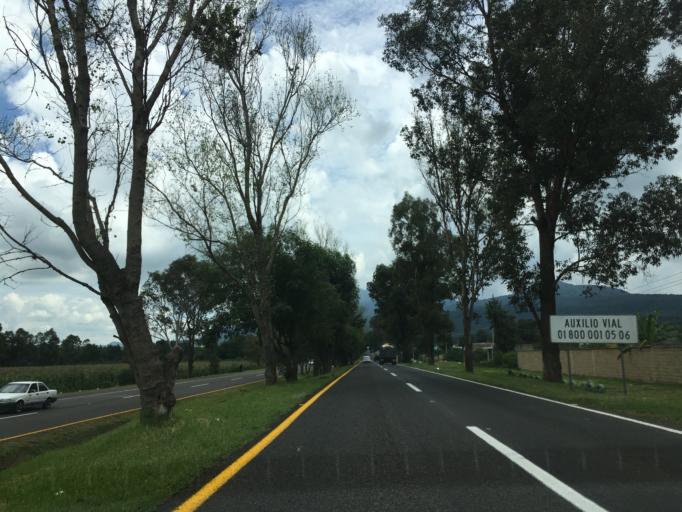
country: MX
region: Michoacan
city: Patzcuaro
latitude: 19.5401
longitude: -101.5790
